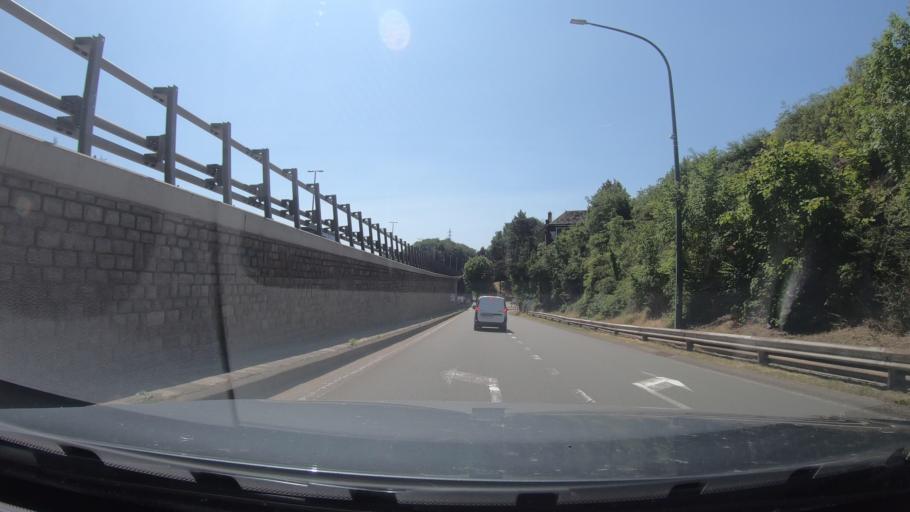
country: BE
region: Wallonia
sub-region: Province de Liege
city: Dison
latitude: 50.6127
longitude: 5.8537
